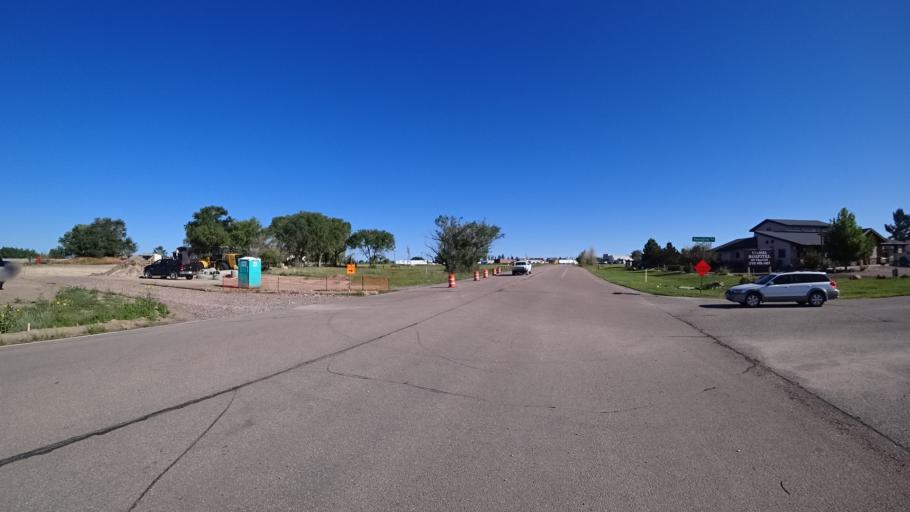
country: US
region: Colorado
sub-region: El Paso County
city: Cimarron Hills
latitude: 38.9300
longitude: -104.6081
